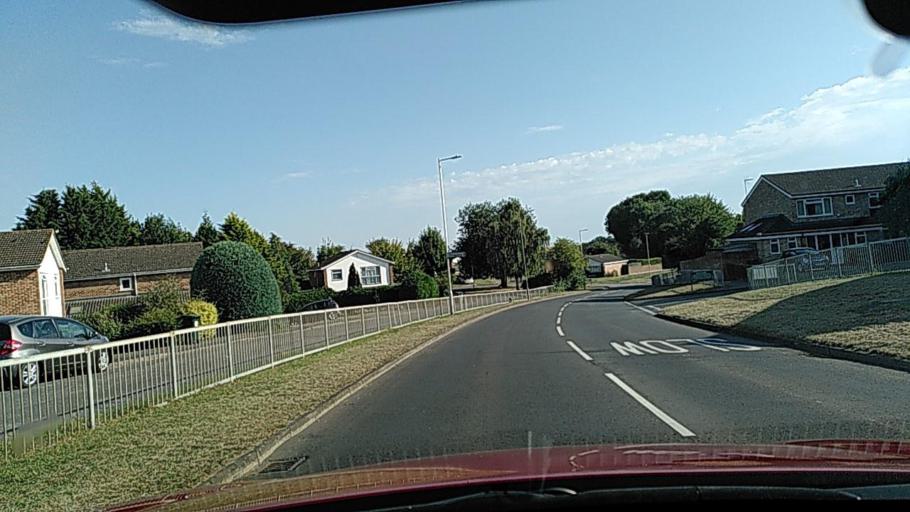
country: GB
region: England
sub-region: Wokingham
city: Sonning
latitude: 51.4831
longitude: -0.9459
